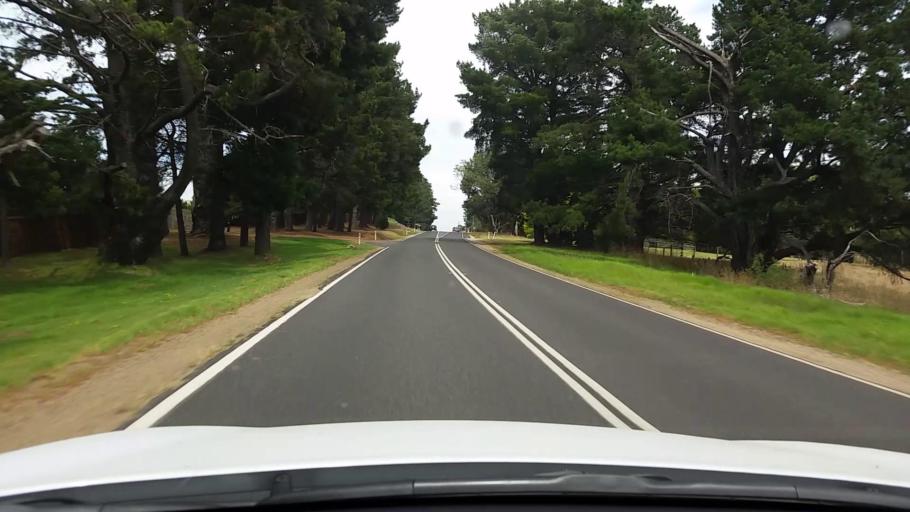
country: AU
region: Victoria
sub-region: Mornington Peninsula
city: Merricks
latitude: -38.4020
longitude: 145.0769
